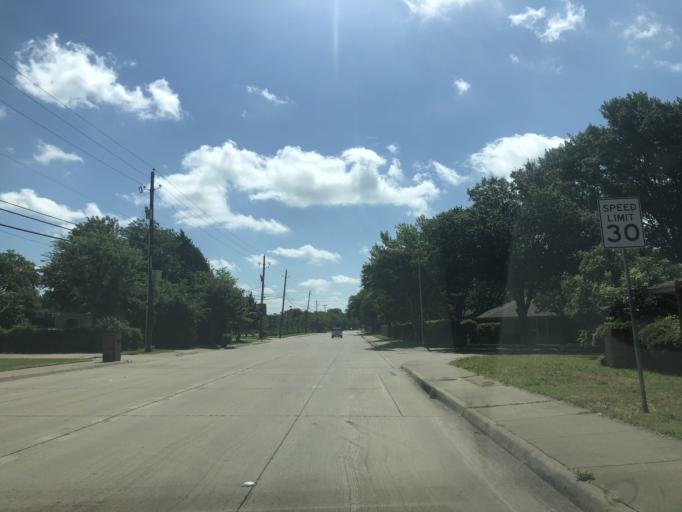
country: US
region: Texas
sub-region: Dallas County
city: Duncanville
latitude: 32.6552
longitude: -96.9286
